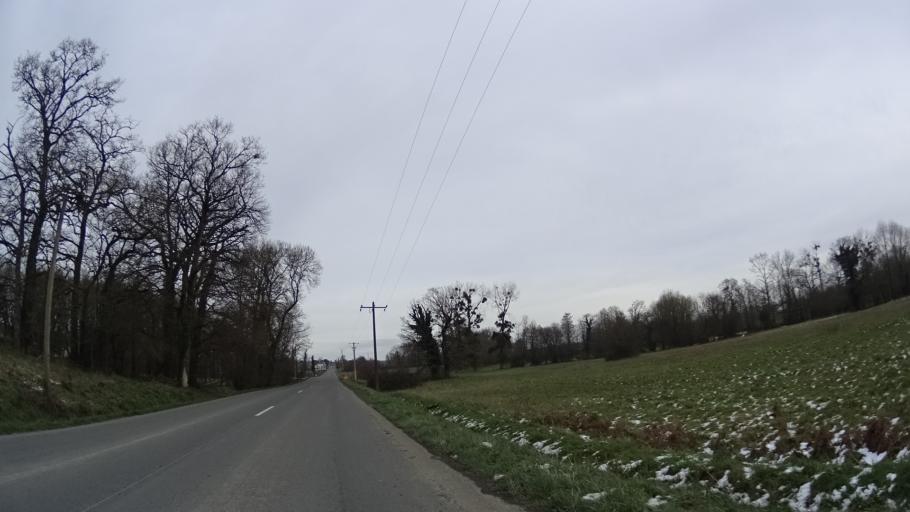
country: FR
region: Brittany
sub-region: Departement d'Ille-et-Vilaine
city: Montauban-de-Bretagne
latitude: 48.2398
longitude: -2.0093
